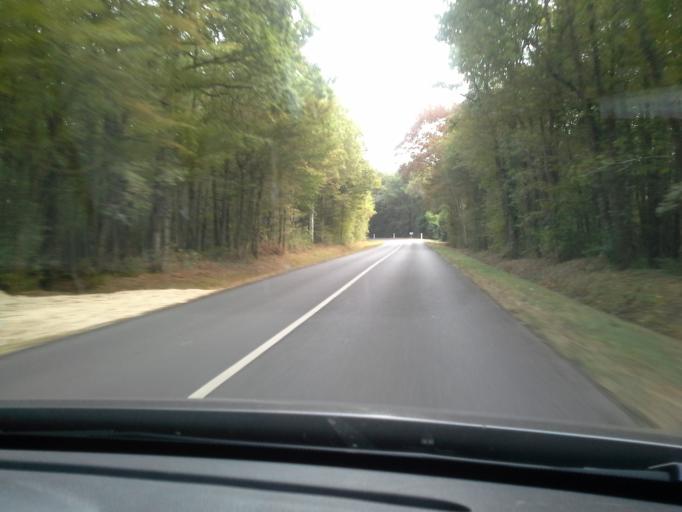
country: FR
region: Centre
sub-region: Departement du Loir-et-Cher
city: Saint-Sulpice-de-Pommeray
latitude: 47.5860
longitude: 1.2027
